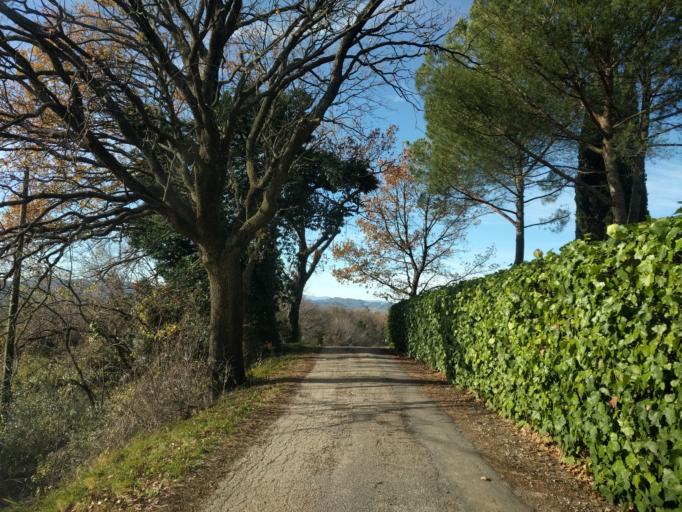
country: IT
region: The Marches
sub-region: Provincia di Pesaro e Urbino
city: Cuccurano
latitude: 43.8096
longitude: 12.9570
